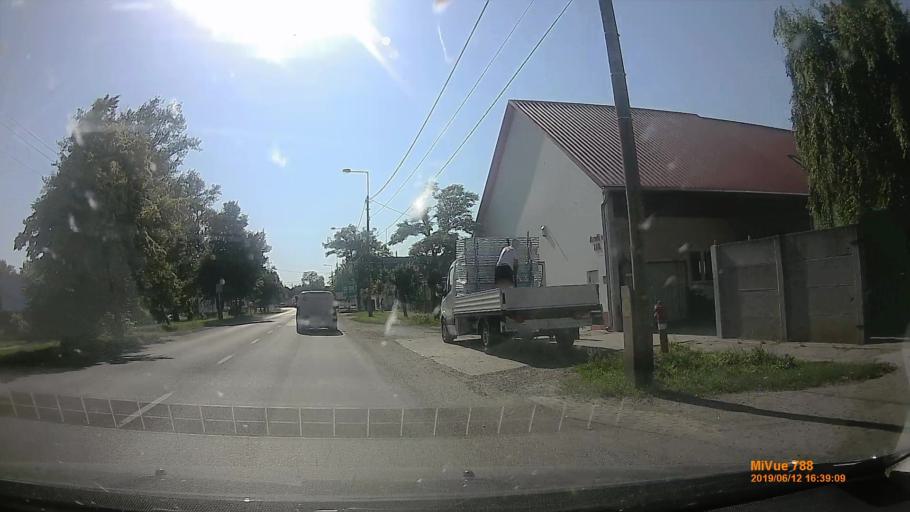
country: HU
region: Csongrad
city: Mako
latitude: 46.2172
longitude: 20.5057
